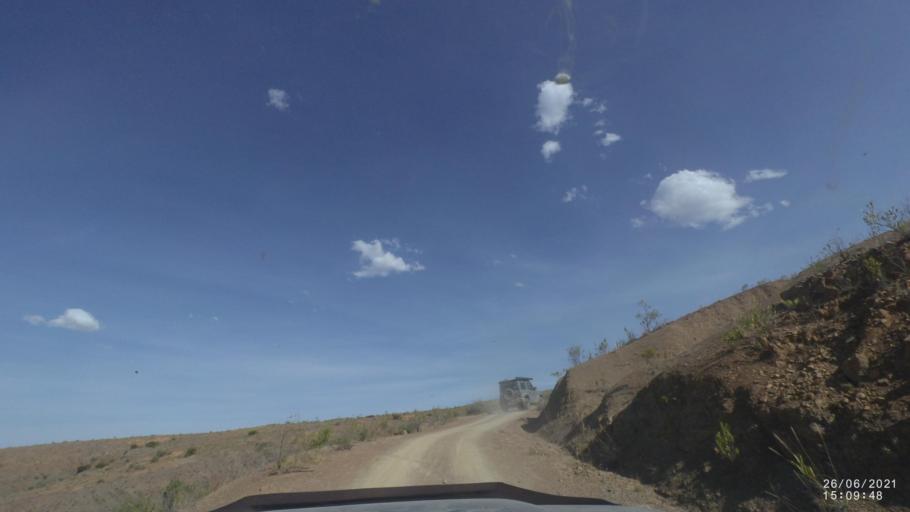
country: BO
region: Cochabamba
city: Mizque
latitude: -17.9519
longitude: -65.6405
